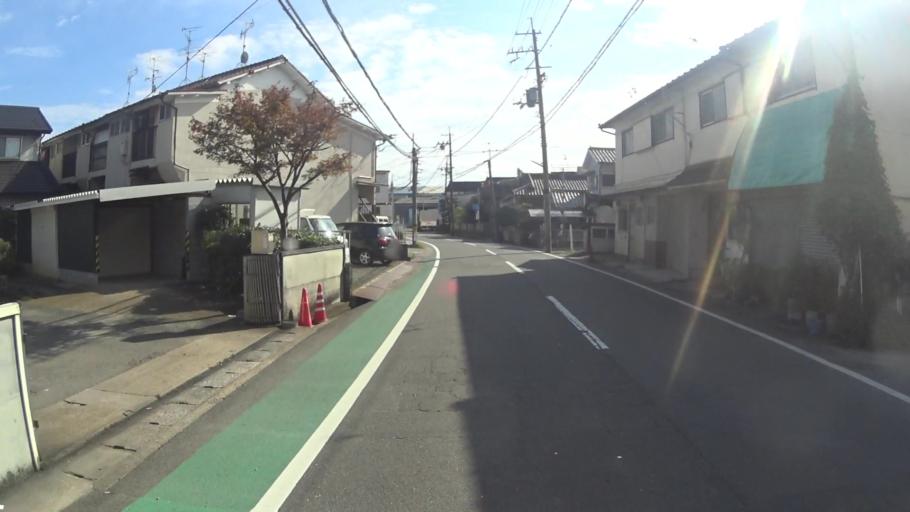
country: JP
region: Kyoto
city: Yawata
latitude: 34.8671
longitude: 135.7296
